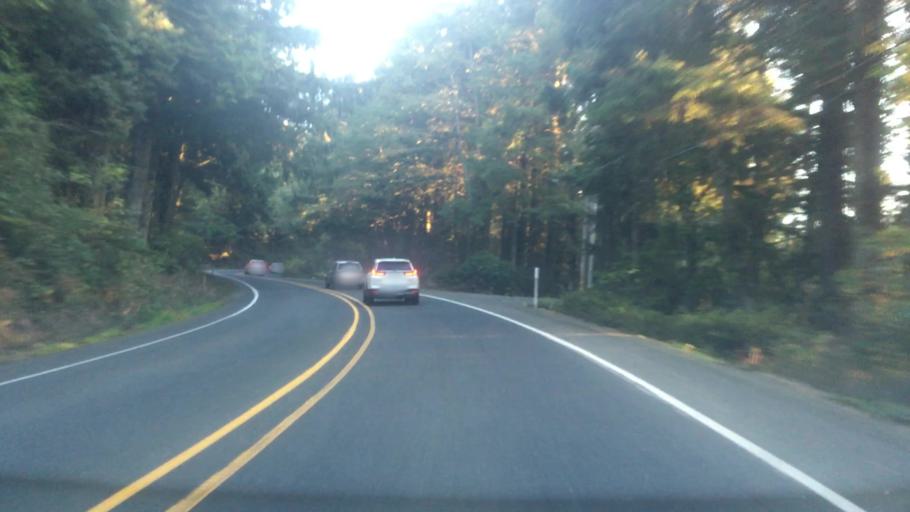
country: US
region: Oregon
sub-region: Clatsop County
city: Cannon Beach
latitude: 45.8423
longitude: -123.9590
